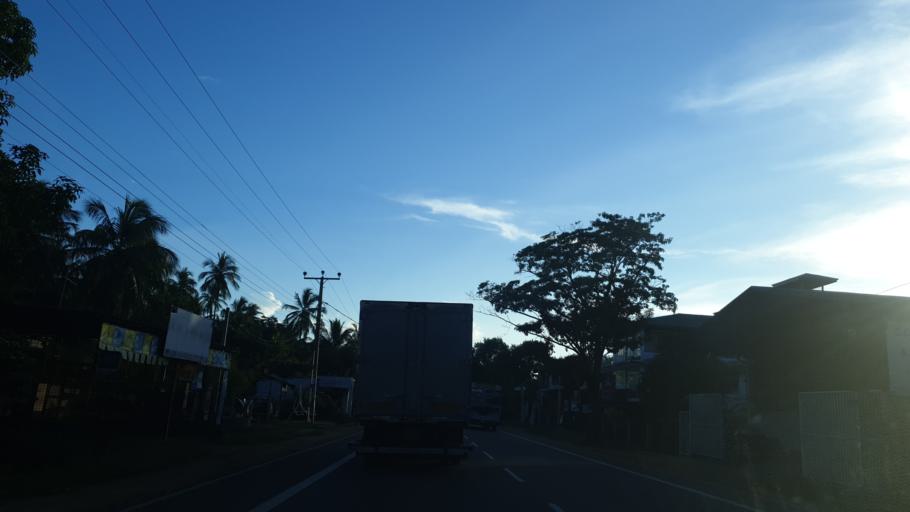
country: LK
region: North Central
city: Anuradhapura
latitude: 8.1465
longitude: 80.2923
